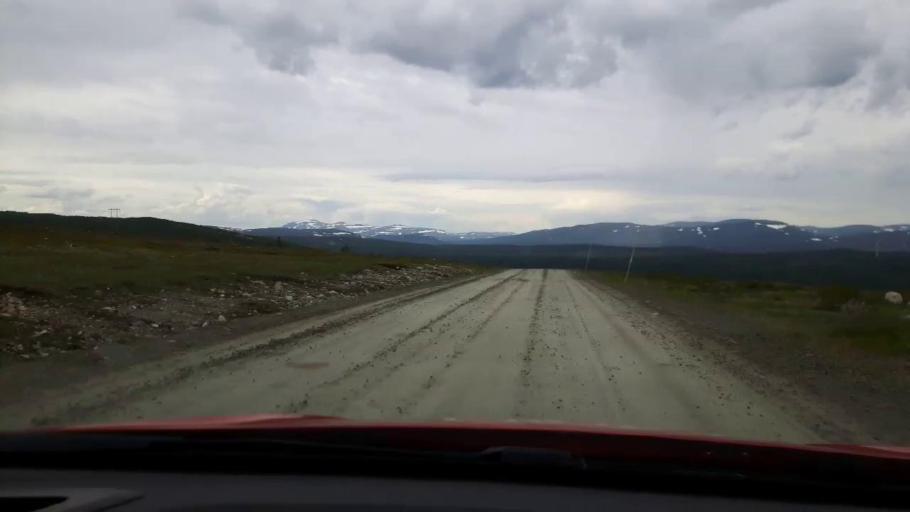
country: SE
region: Jaemtland
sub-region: Are Kommun
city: Are
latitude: 62.7786
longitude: 12.7658
